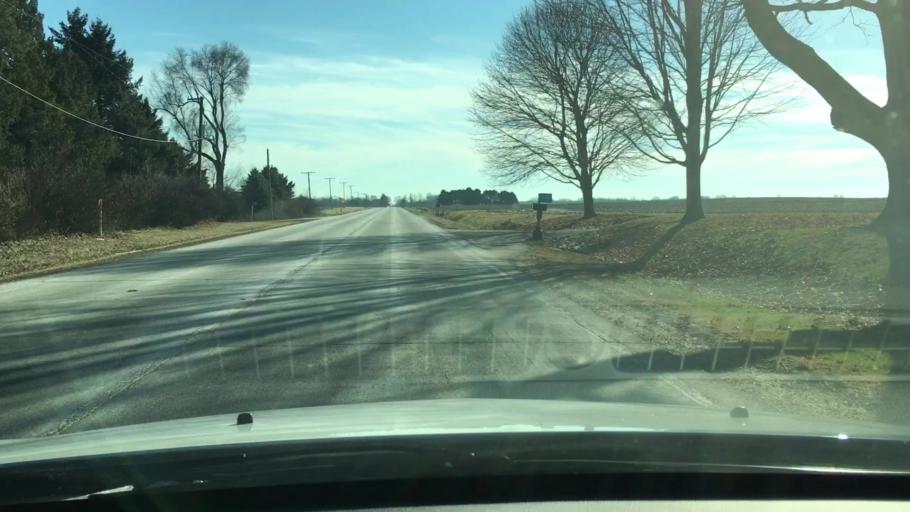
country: US
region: Illinois
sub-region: LaSalle County
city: Mendota
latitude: 41.5819
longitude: -89.1283
